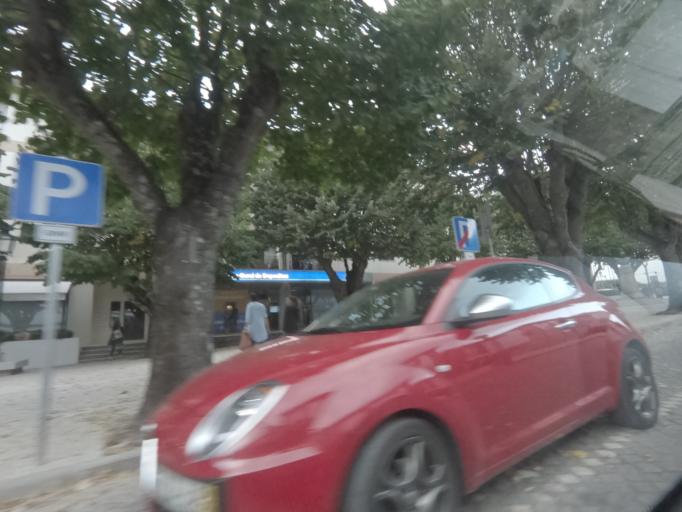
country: PT
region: Vila Real
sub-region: Mesao Frio
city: Mesao Frio
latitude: 41.1594
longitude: -7.8911
